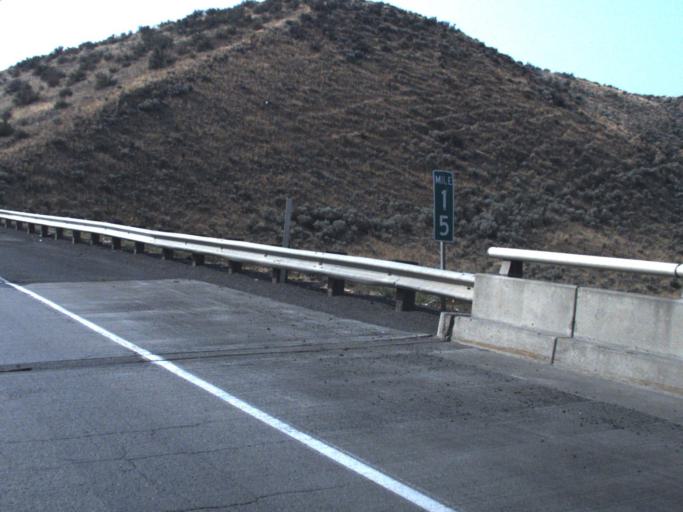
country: US
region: Washington
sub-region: Kittitas County
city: Kittitas
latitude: 46.8003
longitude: -120.3616
